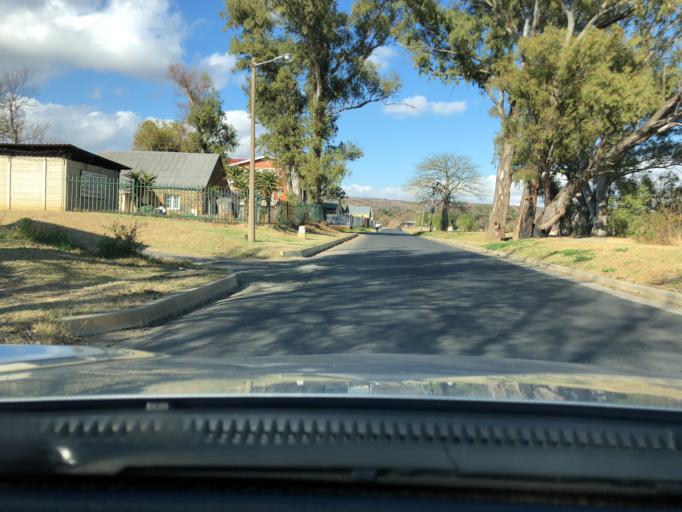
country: ZA
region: KwaZulu-Natal
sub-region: uThukela District Municipality
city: Ladysmith
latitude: -28.5629
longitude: 29.7769
